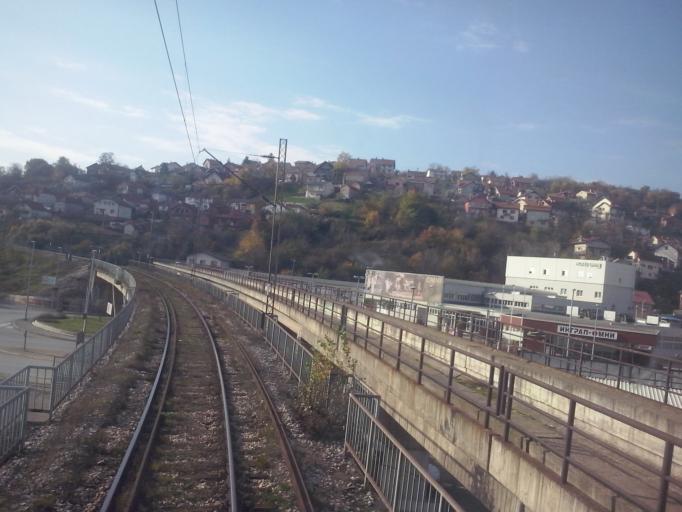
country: RS
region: Central Serbia
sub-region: Kolubarski Okrug
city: Valjevo
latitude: 44.2640
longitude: 19.8922
